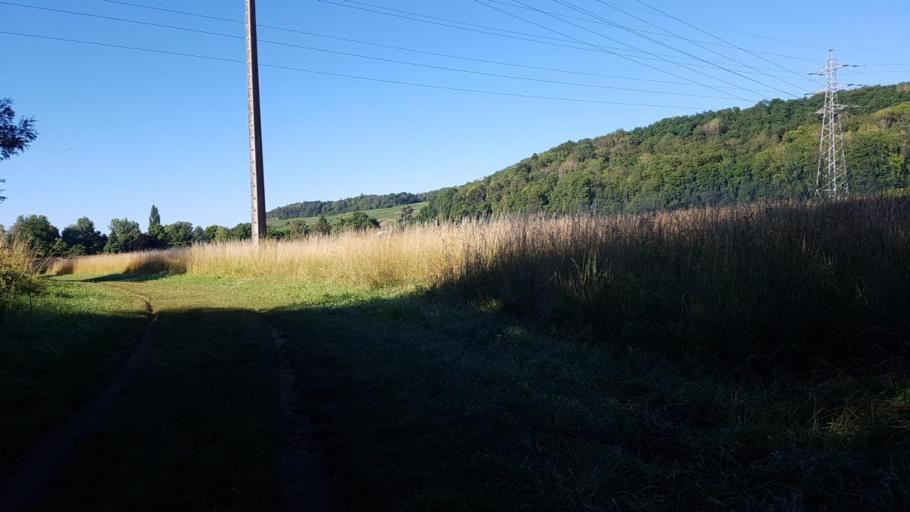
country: FR
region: Picardie
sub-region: Departement de l'Aisne
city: Essomes-sur-Marne
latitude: 49.0221
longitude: 3.3786
